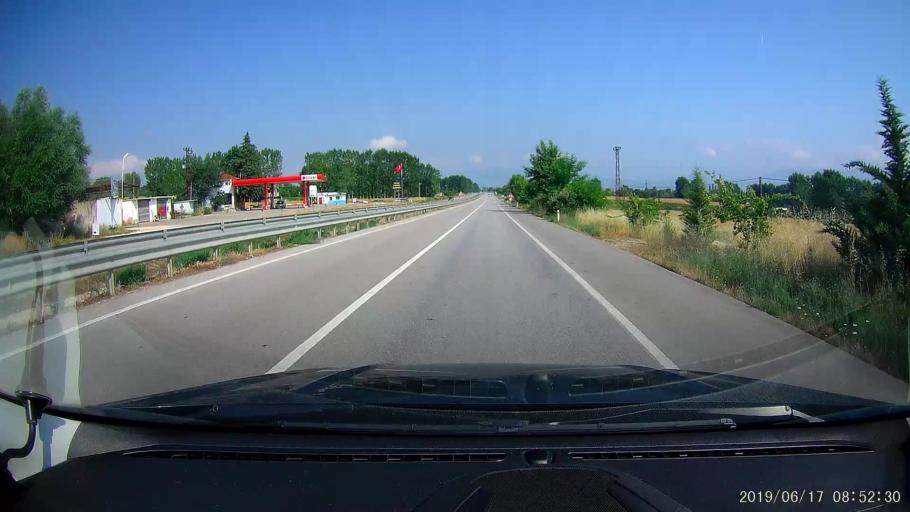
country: TR
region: Tokat
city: Erbaa
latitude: 40.6986
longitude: 36.4955
